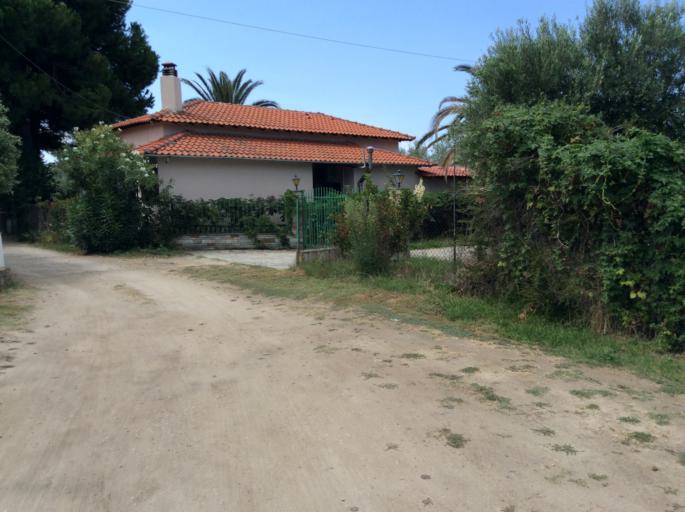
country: GR
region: Central Macedonia
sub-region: Nomos Chalkidikis
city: Sykia
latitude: 39.9901
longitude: 23.9013
